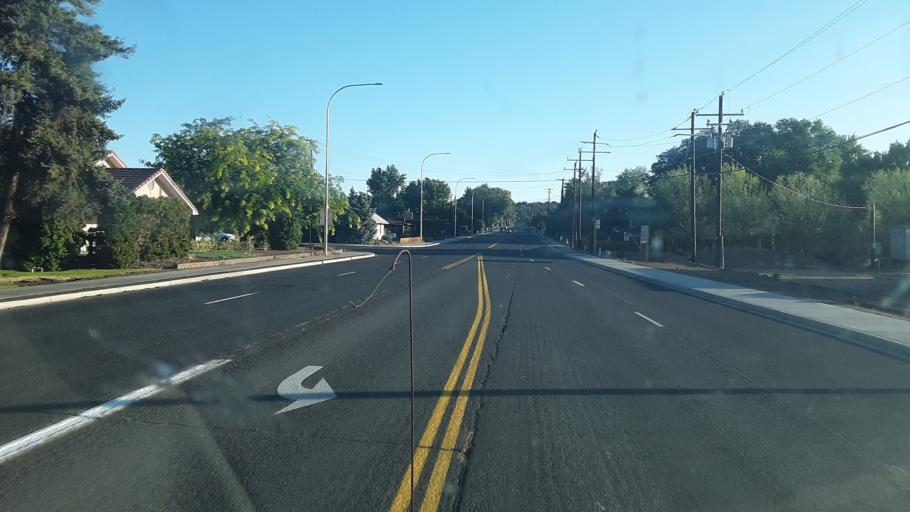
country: US
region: Washington
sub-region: Yakima County
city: West Valley
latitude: 46.5887
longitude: -120.6043
